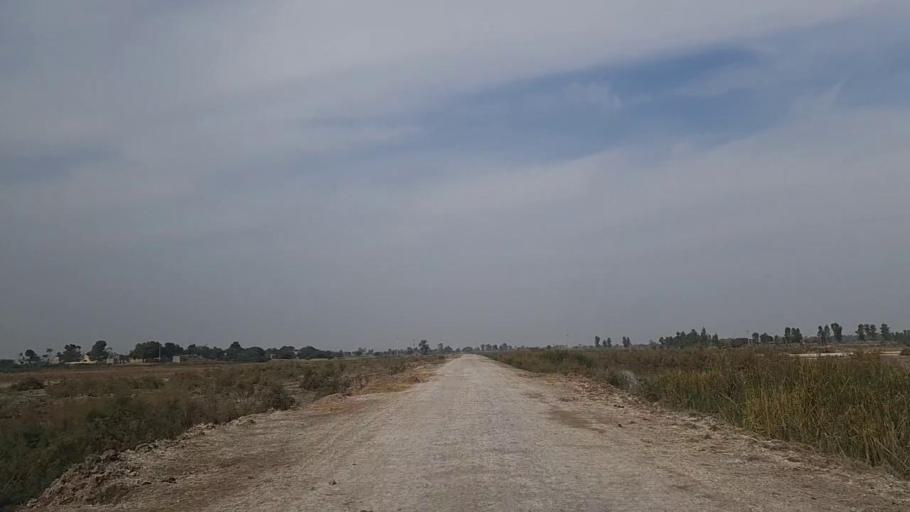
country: PK
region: Sindh
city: Daur
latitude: 26.4792
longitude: 68.4055
